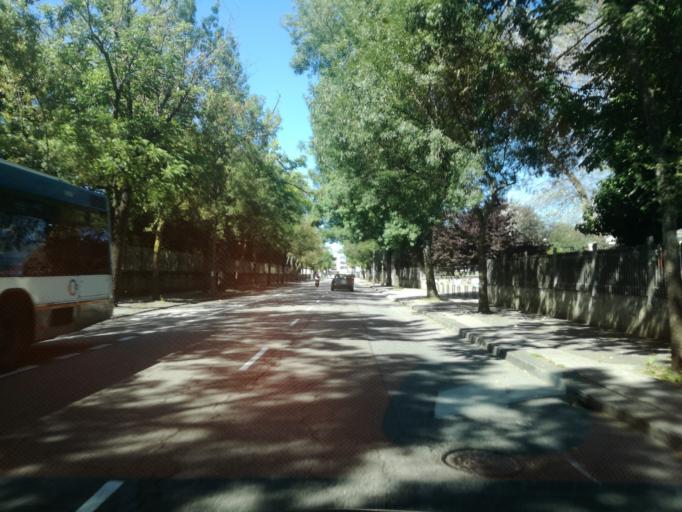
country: PT
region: Porto
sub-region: Matosinhos
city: Sao Mamede de Infesta
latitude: 41.1796
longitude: -8.5984
